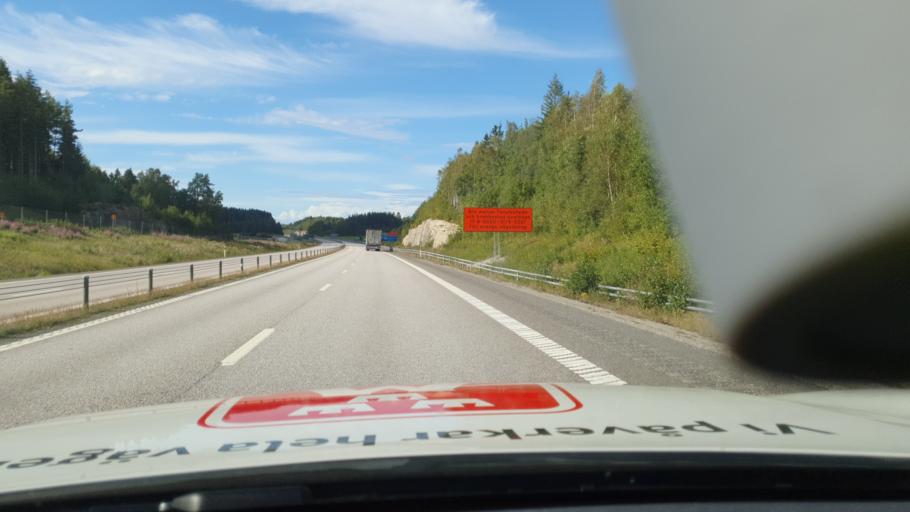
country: SE
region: Vaestra Goetaland
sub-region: Tanums Kommun
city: Tanumshede
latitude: 58.7249
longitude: 11.3486
